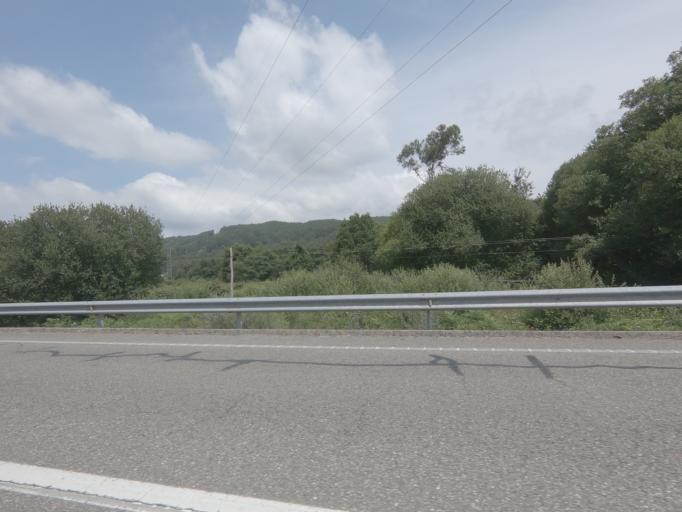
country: ES
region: Galicia
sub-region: Provincia de Pontevedra
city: Tomino
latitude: 42.0246
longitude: -8.7330
